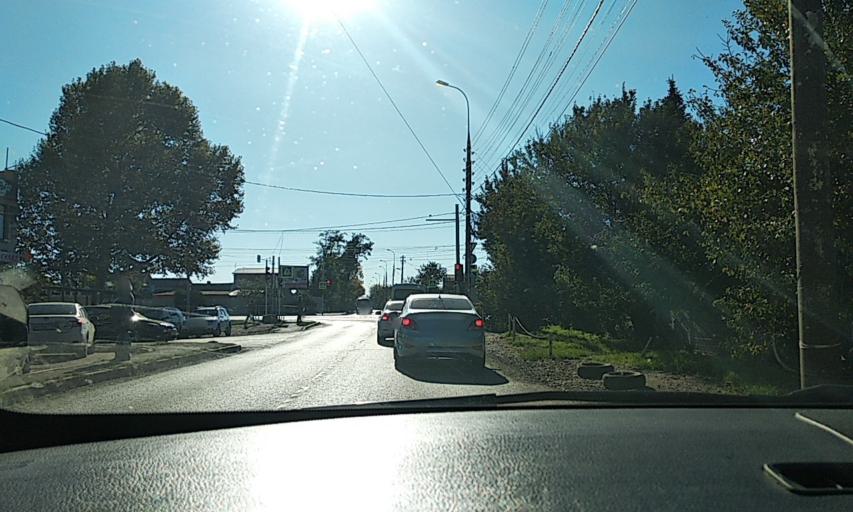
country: RU
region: Krasnodarskiy
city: Pashkovskiy
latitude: 45.0298
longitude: 39.1228
